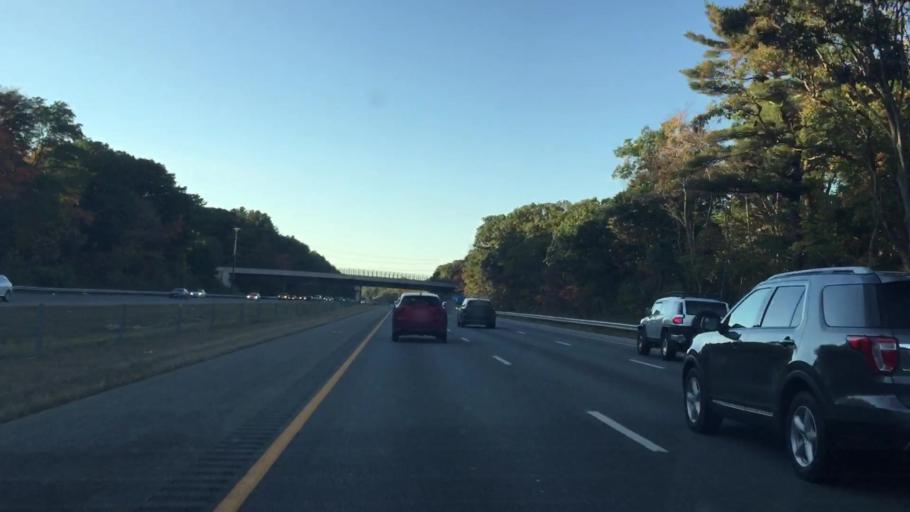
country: US
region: Massachusetts
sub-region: Middlesex County
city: Bedford
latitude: 42.5160
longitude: -71.2571
